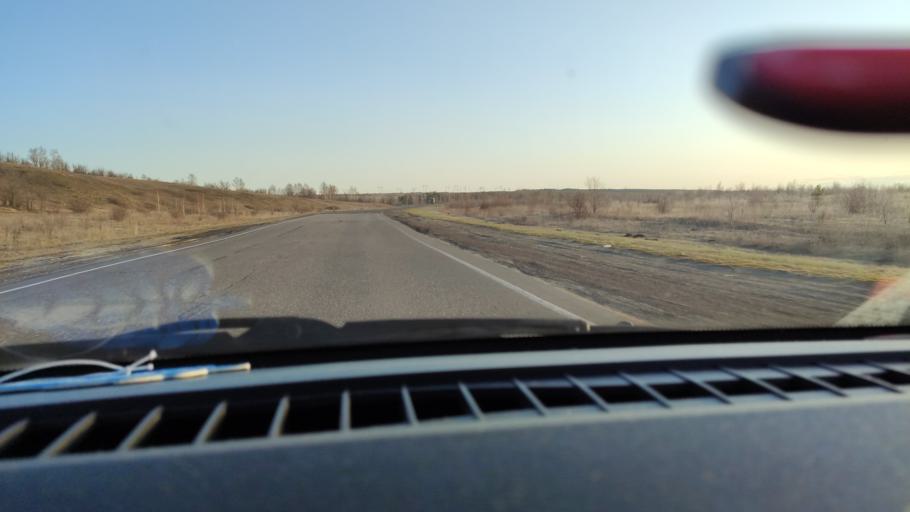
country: RU
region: Saratov
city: Sennoy
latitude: 52.0966
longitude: 46.8127
